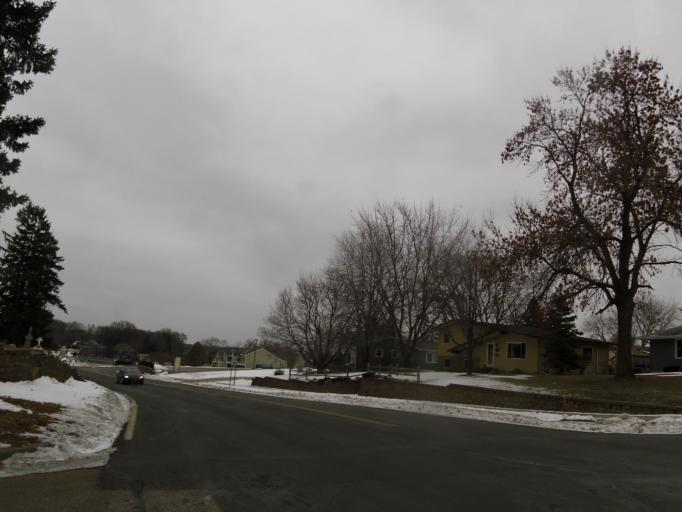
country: US
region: Minnesota
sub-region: Carver County
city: Waconia
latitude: 44.8505
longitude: -93.7785
